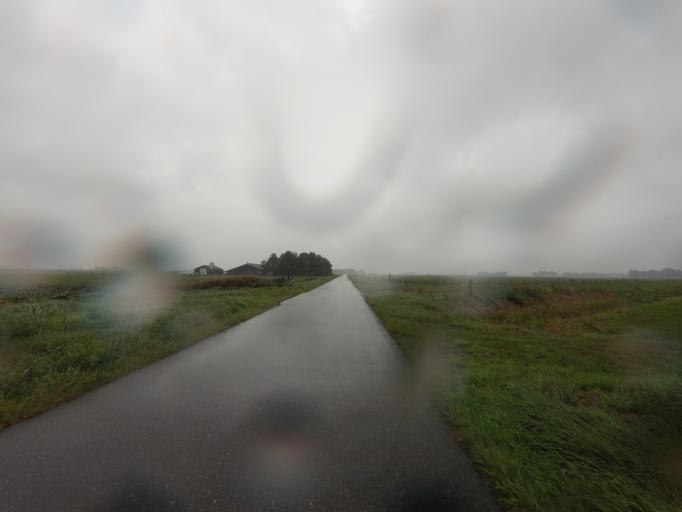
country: NL
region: Friesland
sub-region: Gemeente Boarnsterhim
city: Aldeboarn
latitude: 53.0773
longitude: 5.9358
